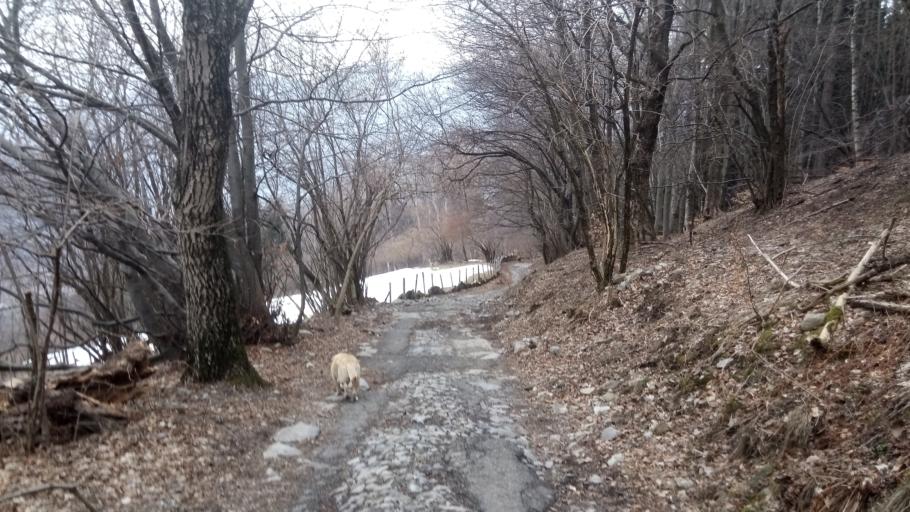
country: IT
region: Lombardy
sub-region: Provincia di Como
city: Occagno
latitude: 45.9117
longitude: 9.1000
